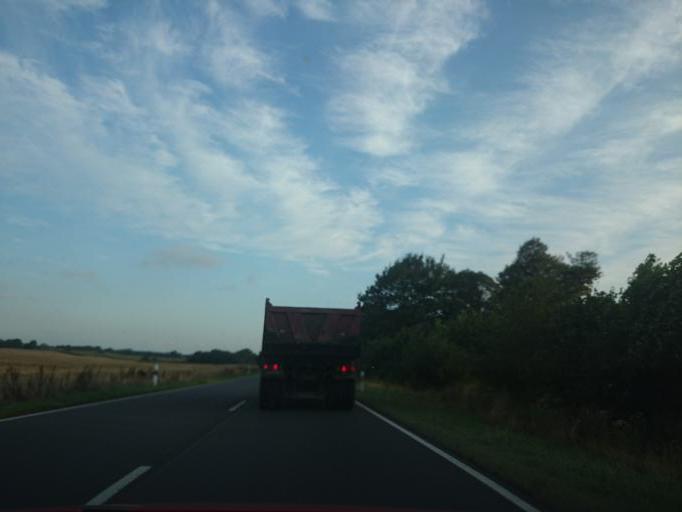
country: DE
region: Mecklenburg-Vorpommern
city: Mesekenhagen
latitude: 54.1965
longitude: 13.2669
